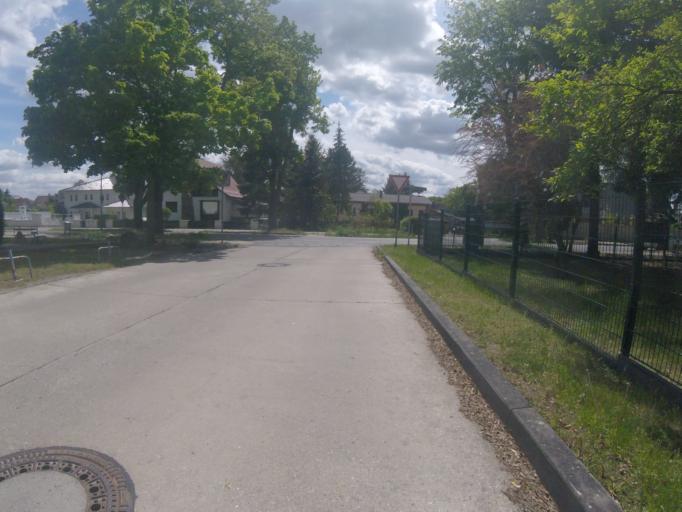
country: DE
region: Brandenburg
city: Konigs Wusterhausen
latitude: 52.2981
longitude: 13.6152
